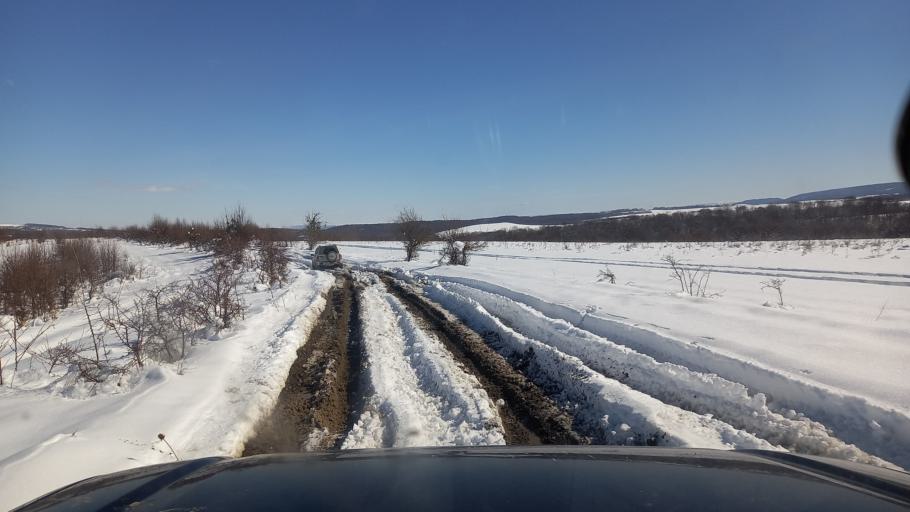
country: RU
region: Krasnodarskiy
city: Gubskaya
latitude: 44.3376
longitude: 40.4295
